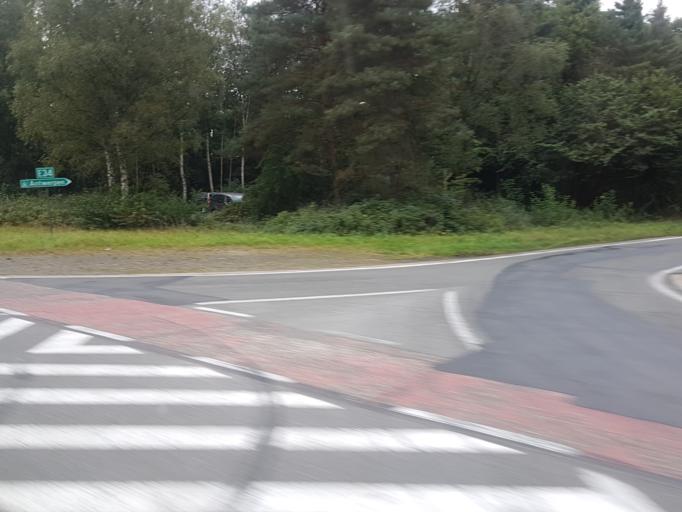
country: BE
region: Flanders
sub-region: Provincie Antwerpen
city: Zandhoven
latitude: 51.2128
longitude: 4.6237
